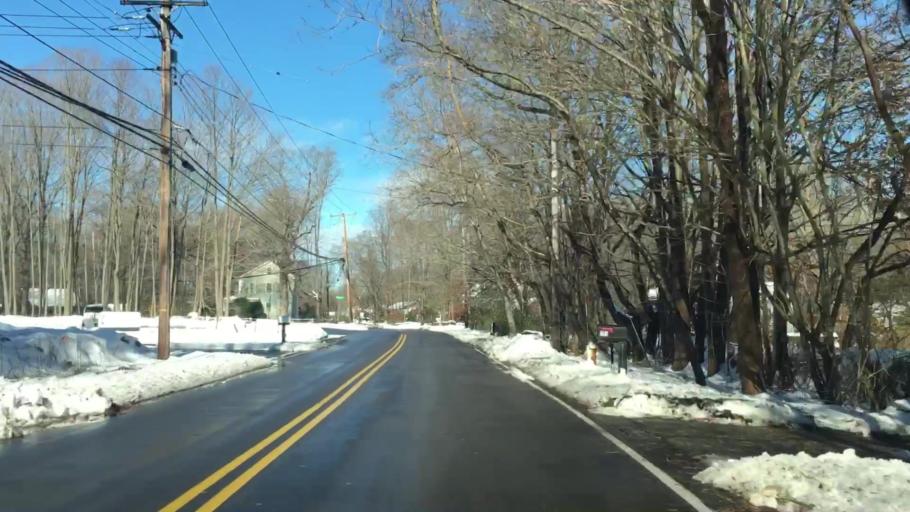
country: US
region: Connecticut
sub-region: Fairfield County
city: Shelton
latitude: 41.3118
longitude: -73.1688
